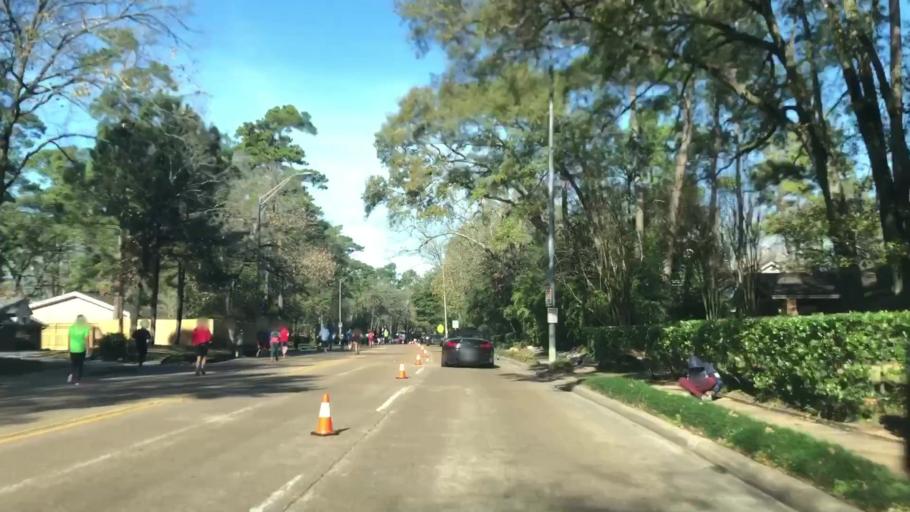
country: US
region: Texas
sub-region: Harris County
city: Hunters Creek Village
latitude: 29.7748
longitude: -95.4812
